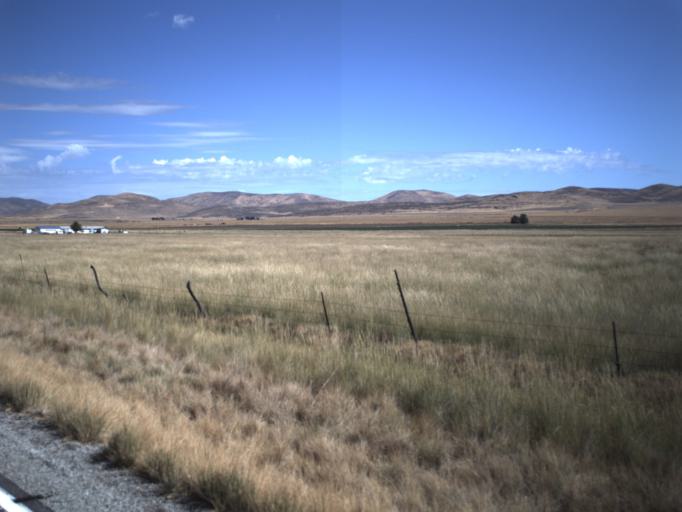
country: US
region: Utah
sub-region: Box Elder County
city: Tremonton
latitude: 41.7624
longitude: -112.4349
